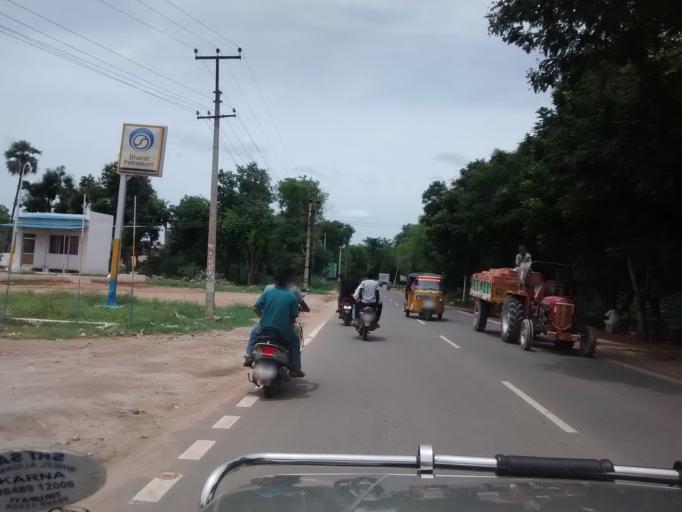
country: IN
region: Andhra Pradesh
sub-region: Chittoor
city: Narasingapuram
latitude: 13.6184
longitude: 79.3630
